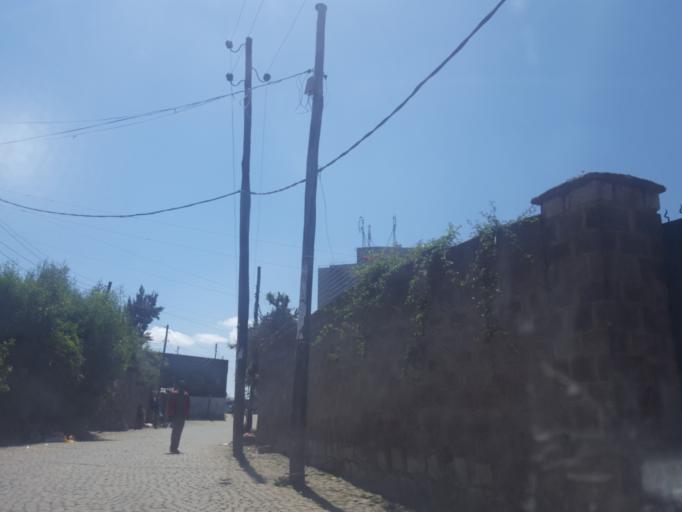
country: ET
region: Adis Abeba
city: Addis Ababa
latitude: 9.0692
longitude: 38.7346
